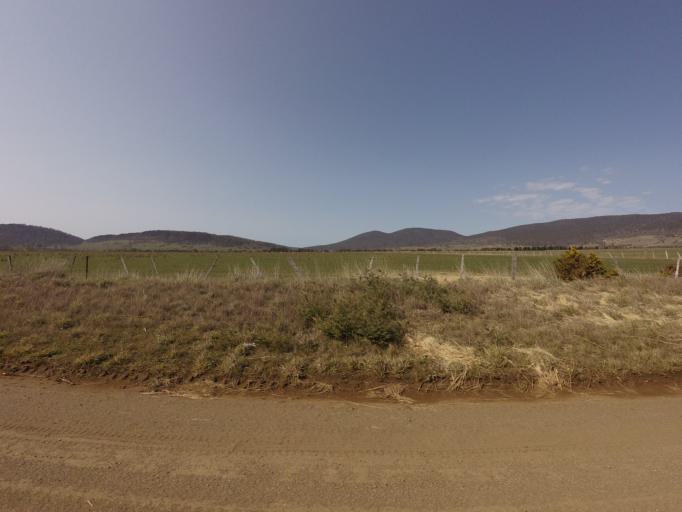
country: AU
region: Tasmania
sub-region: Break O'Day
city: St Helens
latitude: -41.8194
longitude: 147.9356
